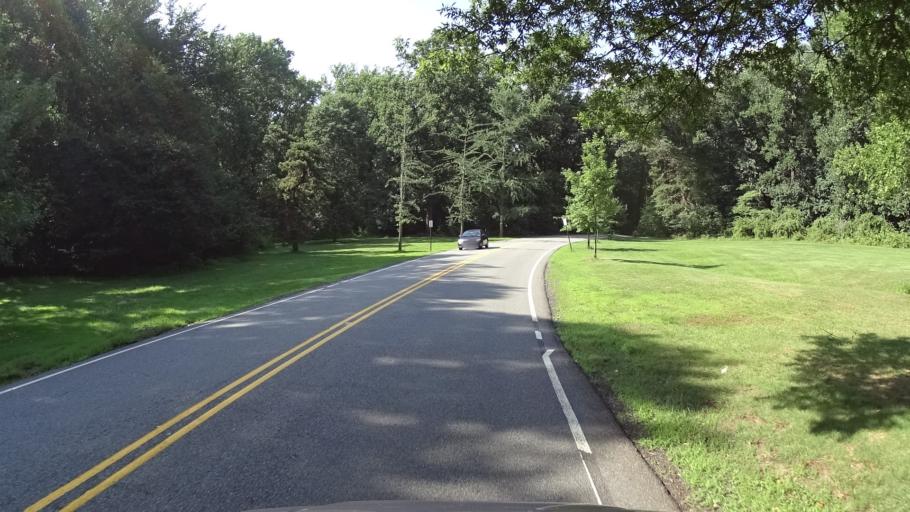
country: US
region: New Jersey
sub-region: Union County
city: Mountainside
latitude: 40.6882
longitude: -74.3728
